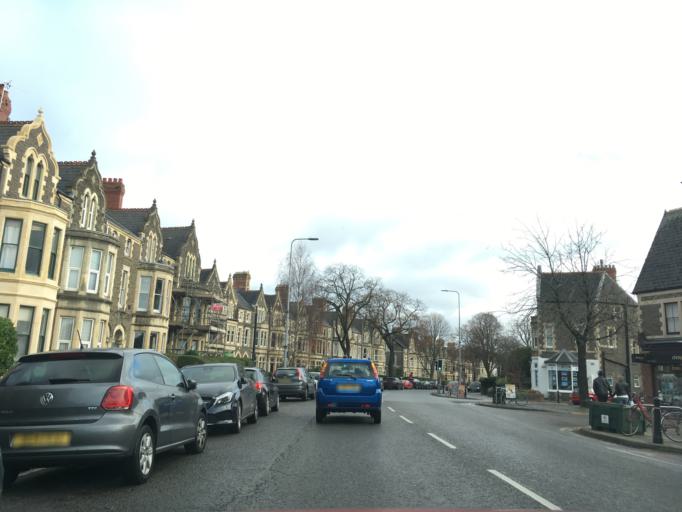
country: GB
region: Wales
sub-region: Cardiff
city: Cardiff
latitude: 51.4888
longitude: -3.2007
